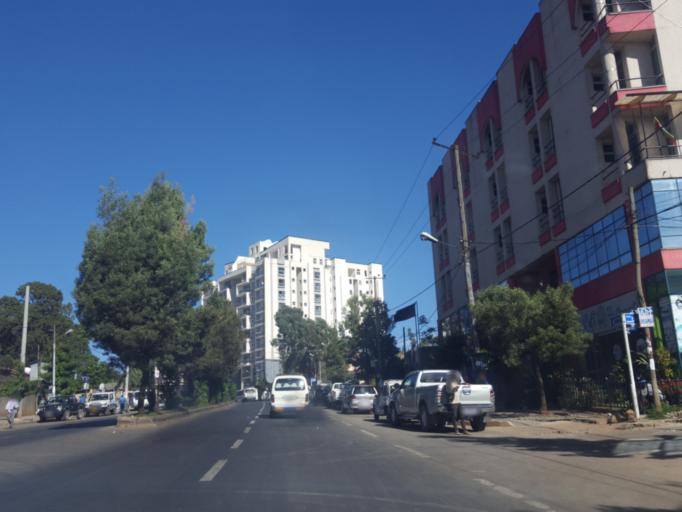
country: ET
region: Adis Abeba
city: Addis Ababa
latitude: 9.0567
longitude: 38.7406
